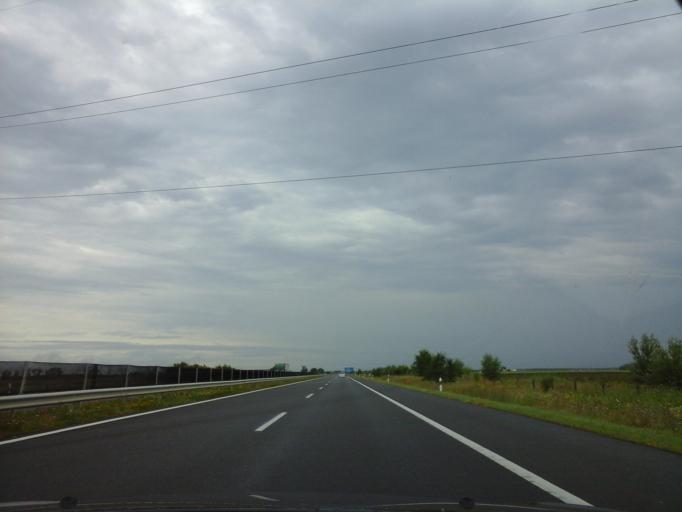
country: HU
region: Hajdu-Bihar
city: Polgar
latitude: 47.8331
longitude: 21.1516
